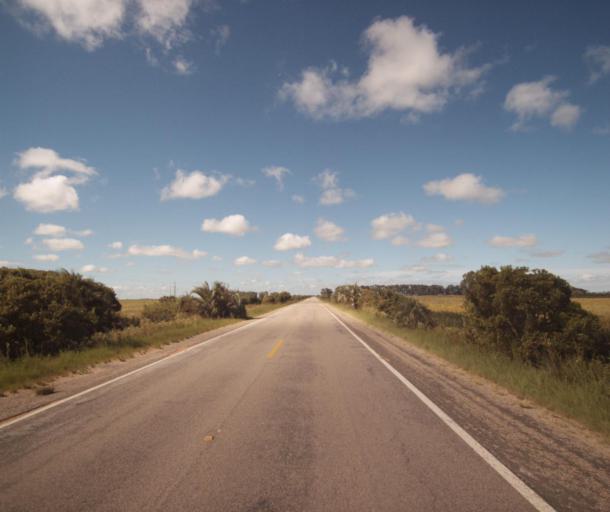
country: BR
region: Rio Grande do Sul
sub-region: Santa Vitoria Do Palmar
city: Santa Vitoria do Palmar
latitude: -33.4131
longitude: -53.2314
